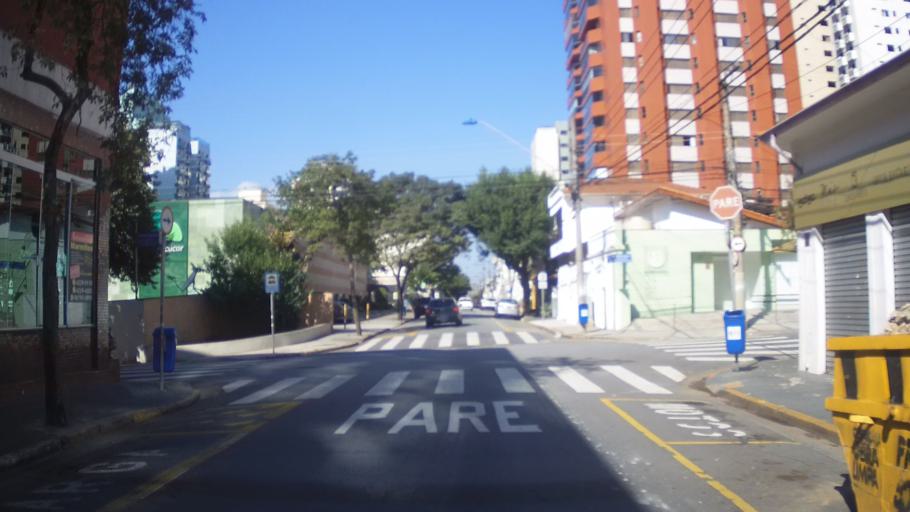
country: BR
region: Sao Paulo
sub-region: Sao Caetano Do Sul
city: Sao Caetano do Sul
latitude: -23.6210
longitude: -46.5646
